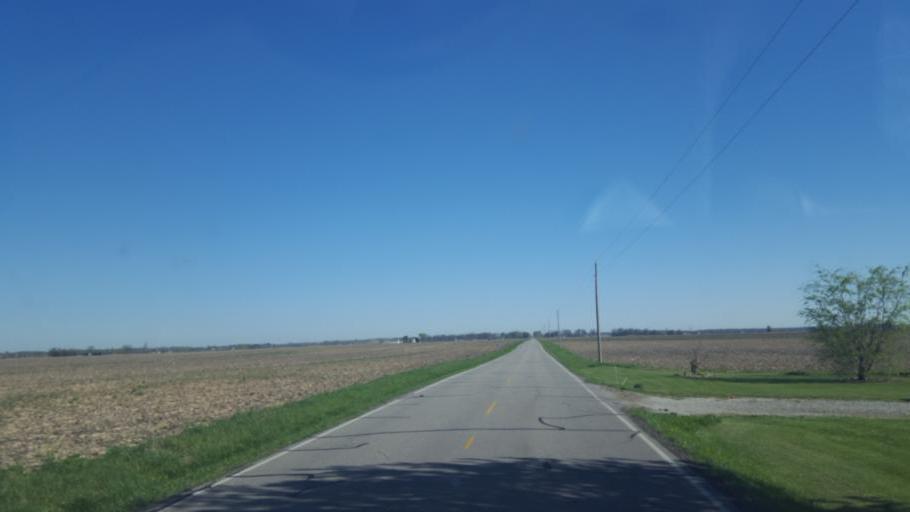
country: US
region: Ohio
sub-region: Marion County
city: Marion
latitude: 40.7069
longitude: -83.0922
